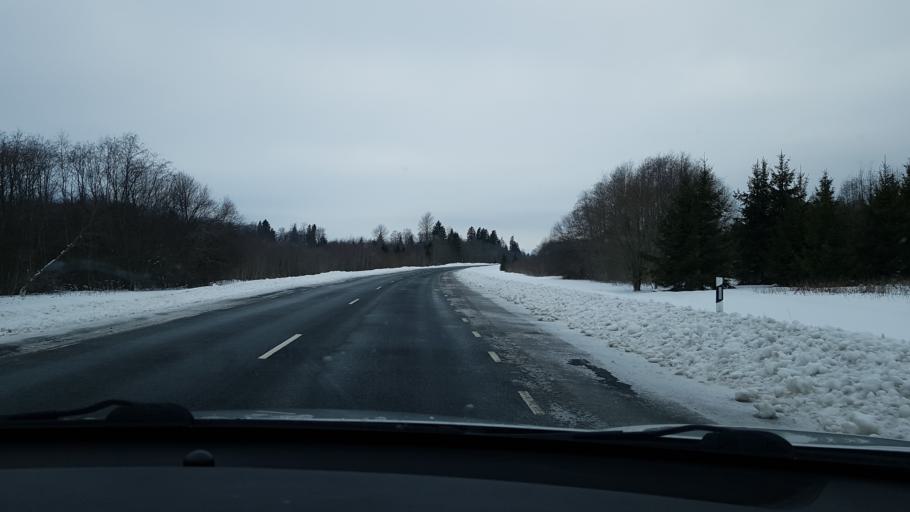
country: EE
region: Jaervamaa
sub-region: Jaerva-Jaani vald
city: Jarva-Jaani
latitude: 58.8973
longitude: 25.7900
